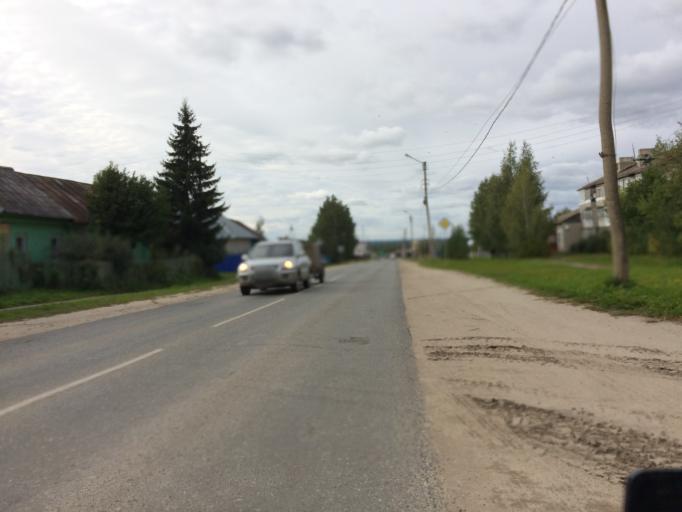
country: RU
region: Mariy-El
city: Yoshkar-Ola
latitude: 56.6562
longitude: 47.9750
